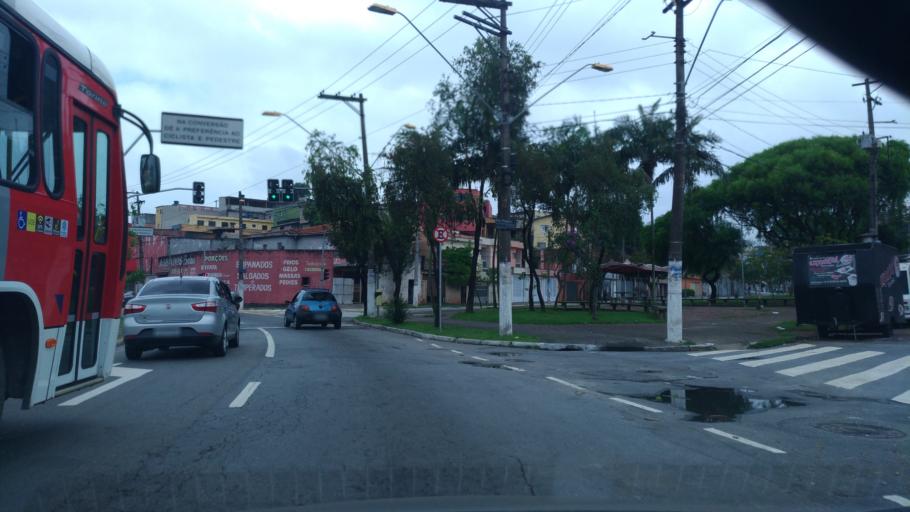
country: BR
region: Sao Paulo
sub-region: Santo Andre
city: Santo Andre
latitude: -23.6935
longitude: -46.5099
